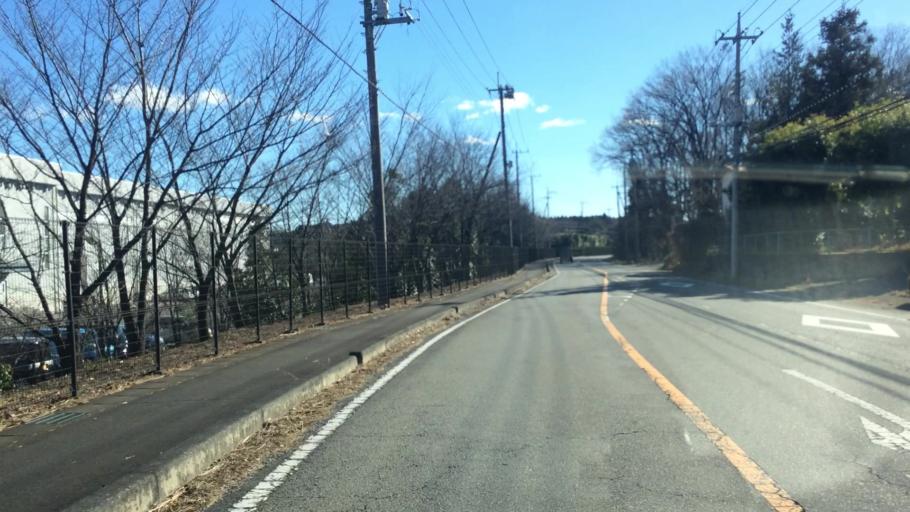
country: JP
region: Tochigi
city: Imaichi
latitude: 36.7592
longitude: 139.7286
